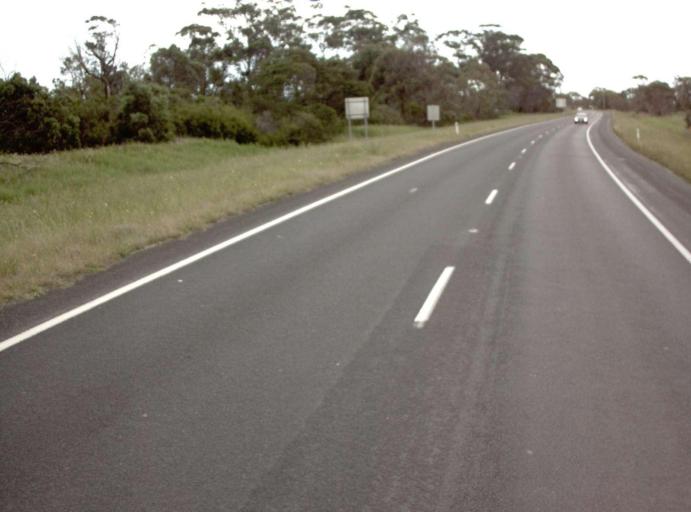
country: AU
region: Victoria
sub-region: Casey
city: Tooradin
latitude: -38.2137
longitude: 145.4196
